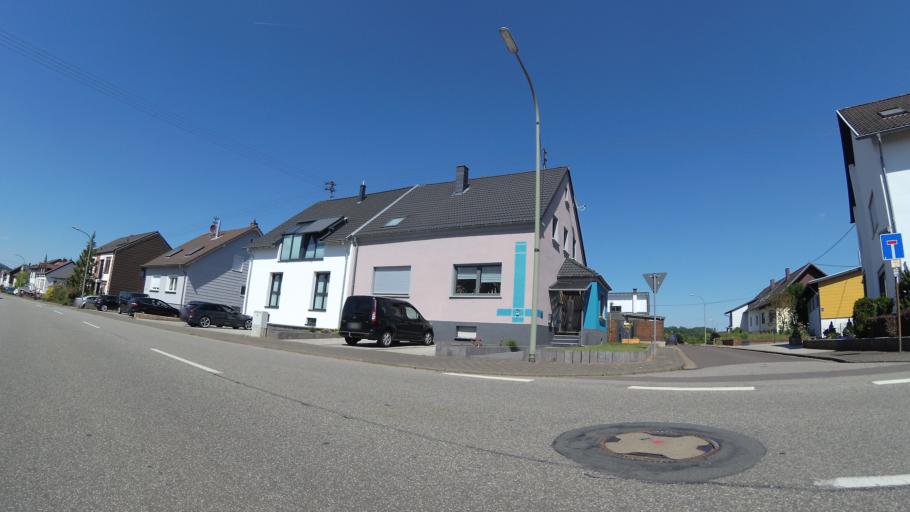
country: DE
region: Saarland
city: Saarwellingen
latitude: 49.3469
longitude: 6.8105
